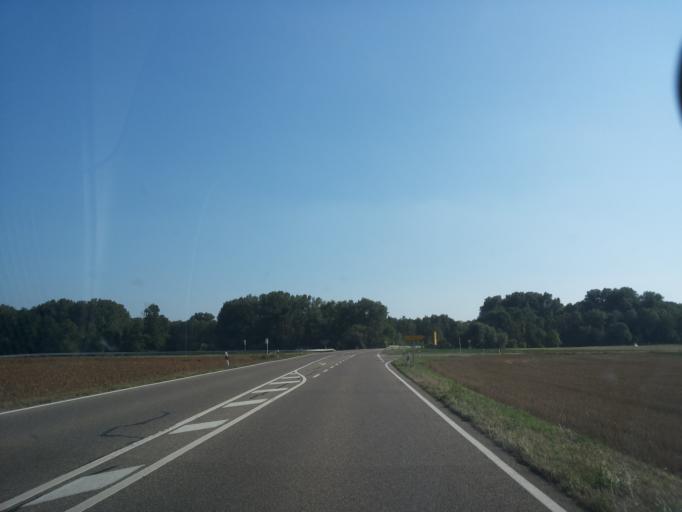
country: DE
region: Bavaria
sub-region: Upper Bavaria
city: Munchsmunster
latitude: 48.8147
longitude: 11.7014
